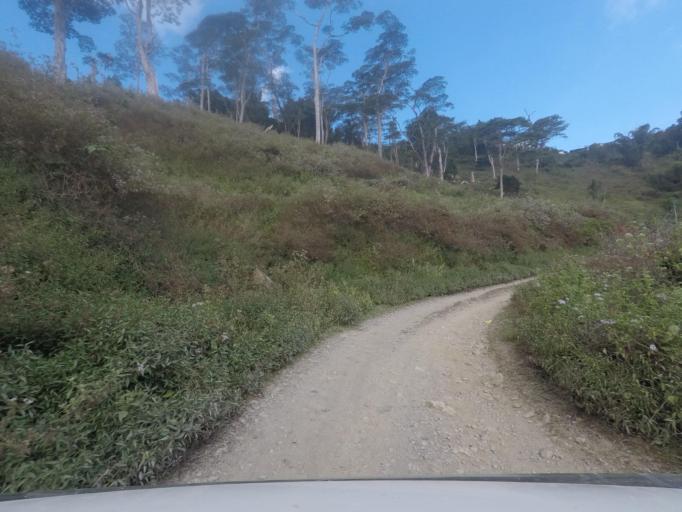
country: TL
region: Ermera
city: Gleno
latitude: -8.7499
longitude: 125.3257
